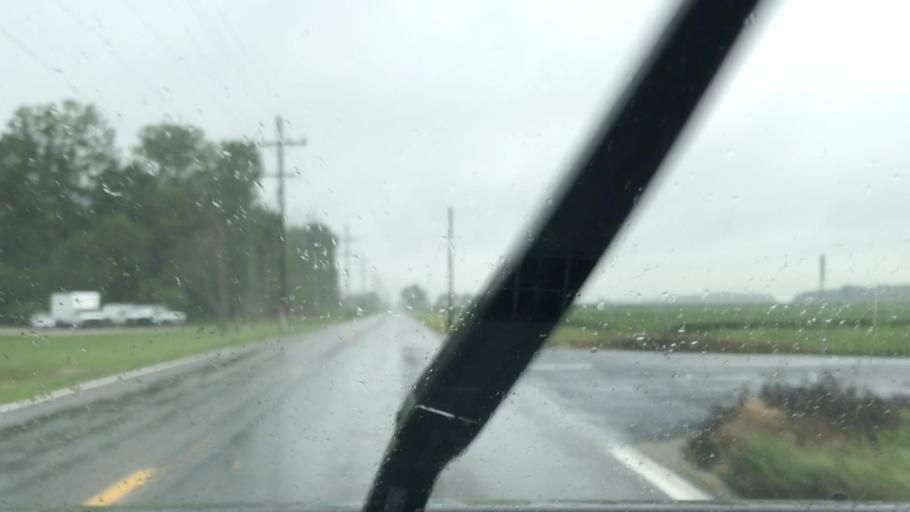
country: US
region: Indiana
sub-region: Hamilton County
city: Sheridan
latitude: 40.1298
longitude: -86.2320
